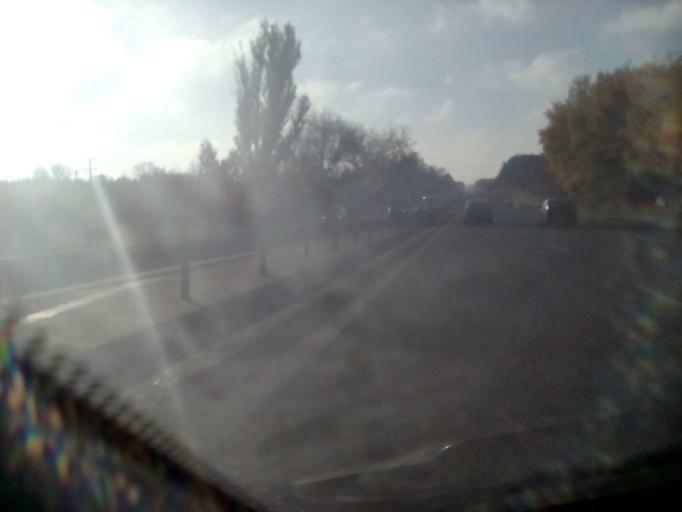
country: PL
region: Masovian Voivodeship
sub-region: Powiat piaseczynski
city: Tarczyn
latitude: 51.9261
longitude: 20.8508
